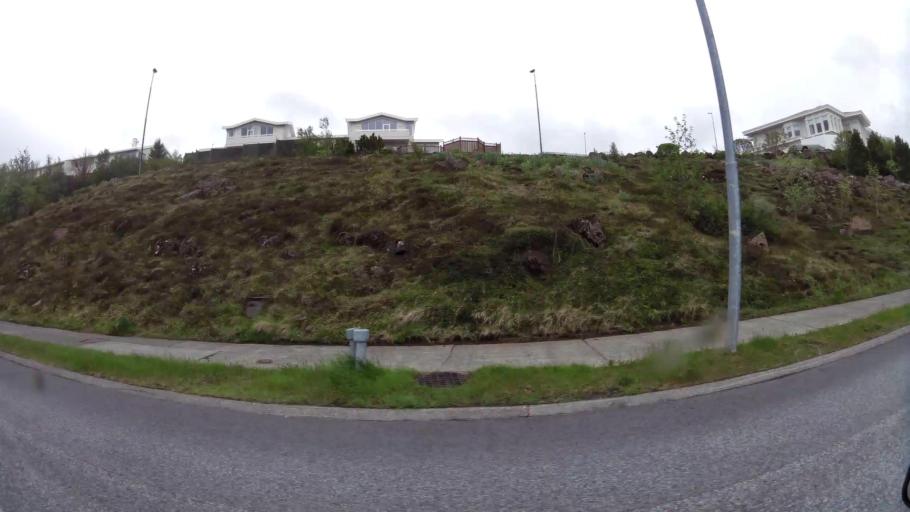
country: IS
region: Capital Region
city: Hafnarfjoerdur
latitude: 64.0614
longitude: -21.9248
